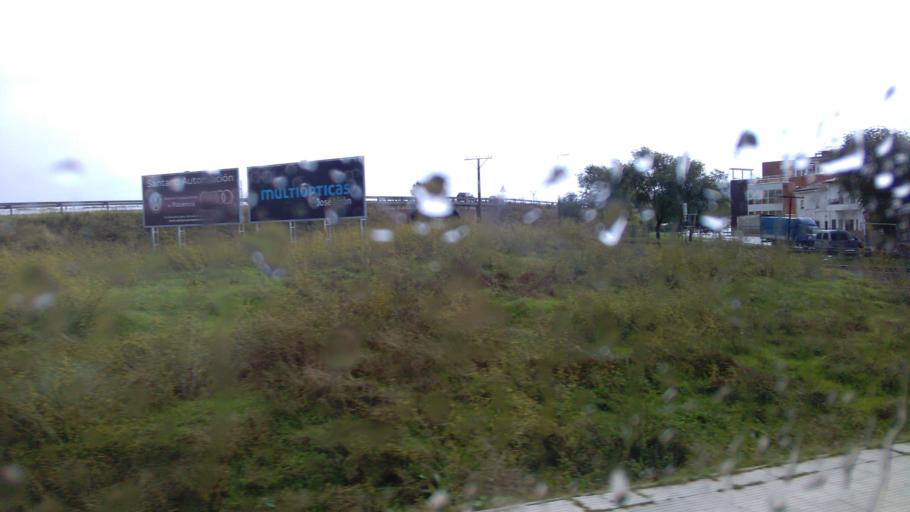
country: ES
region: Extremadura
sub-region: Provincia de Caceres
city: Navalmoral de la Mata
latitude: 39.8966
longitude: -5.5373
